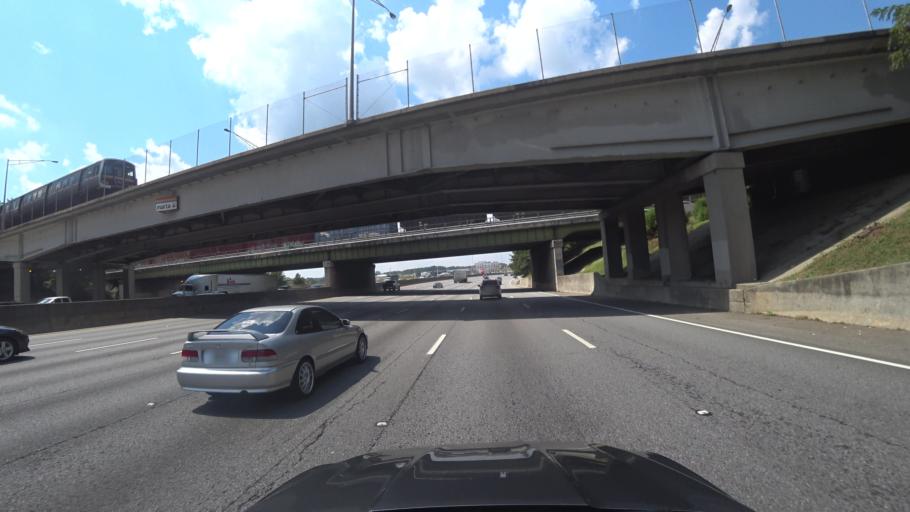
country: US
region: Georgia
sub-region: DeKalb County
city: Doraville
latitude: 33.9049
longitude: -84.2770
